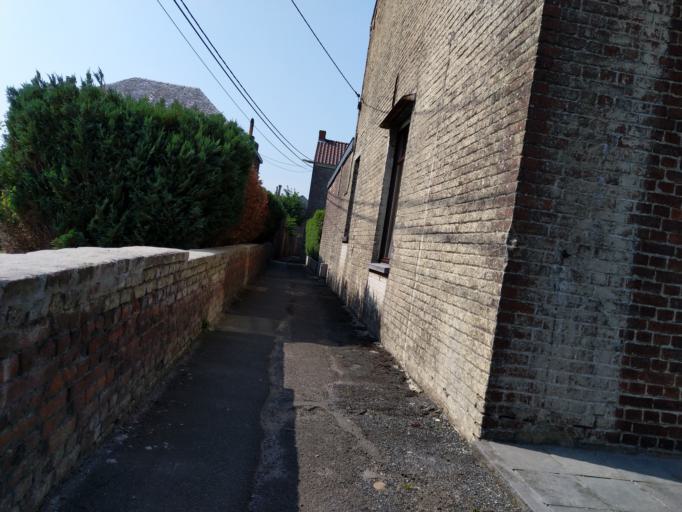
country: BE
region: Wallonia
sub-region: Province du Hainaut
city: Soignies
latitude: 50.5669
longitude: 4.0034
